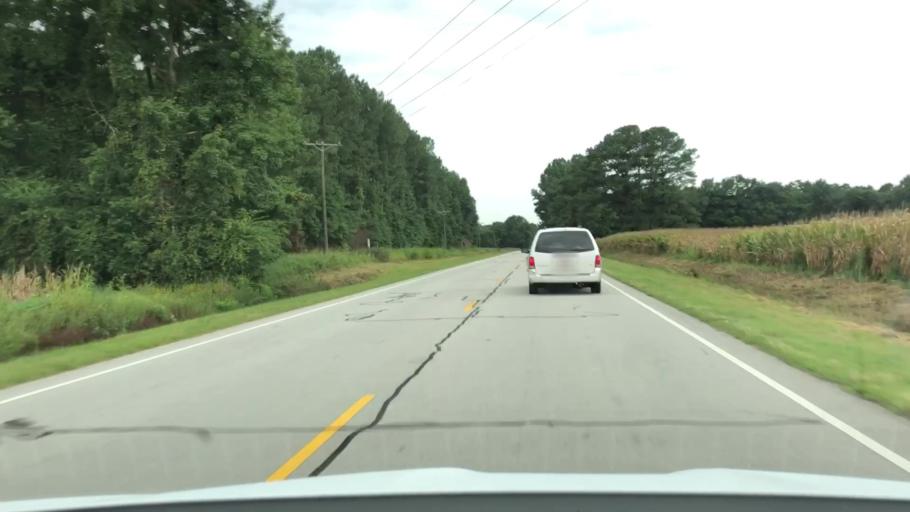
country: US
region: North Carolina
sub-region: Jones County
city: Trenton
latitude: 35.0787
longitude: -77.4077
